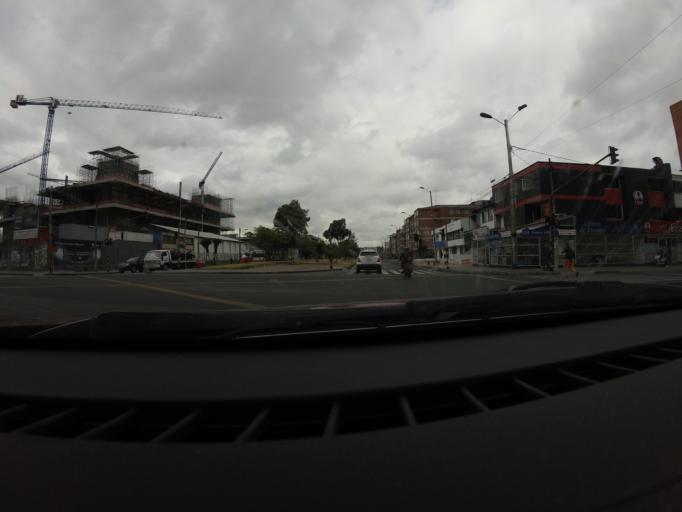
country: CO
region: Bogota D.C.
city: Bogota
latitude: 4.6302
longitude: -74.0939
